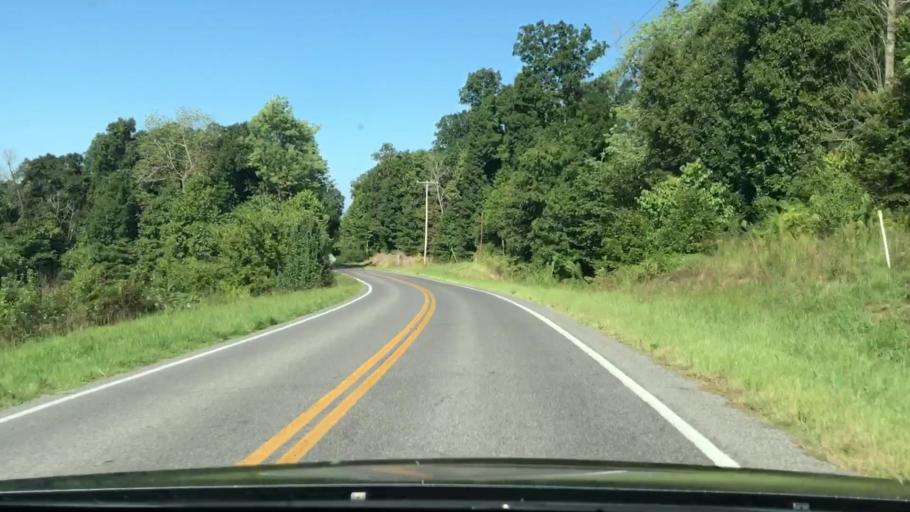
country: US
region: Kentucky
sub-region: Graves County
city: Mayfield
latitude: 36.7792
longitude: -88.5137
